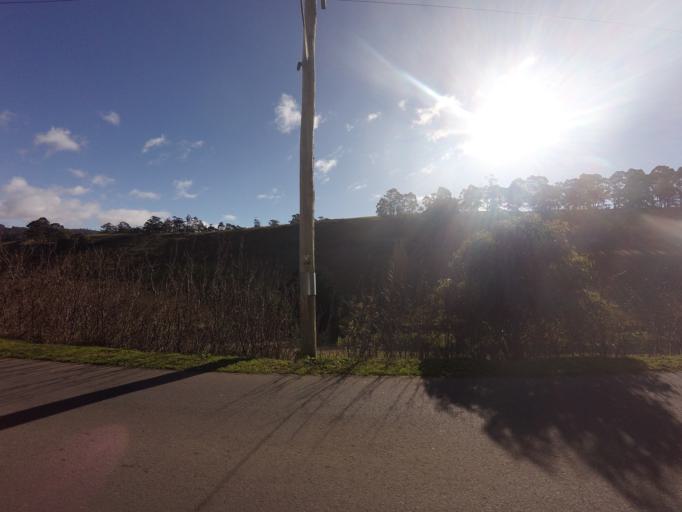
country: AU
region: Tasmania
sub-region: Glenorchy
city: Berriedale
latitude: -42.8336
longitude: 147.2034
